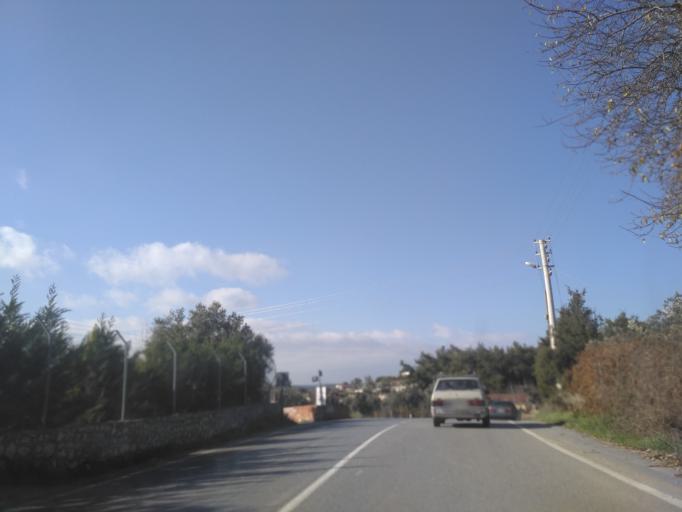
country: TR
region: Izmir
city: Buca
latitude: 38.3529
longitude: 27.2520
